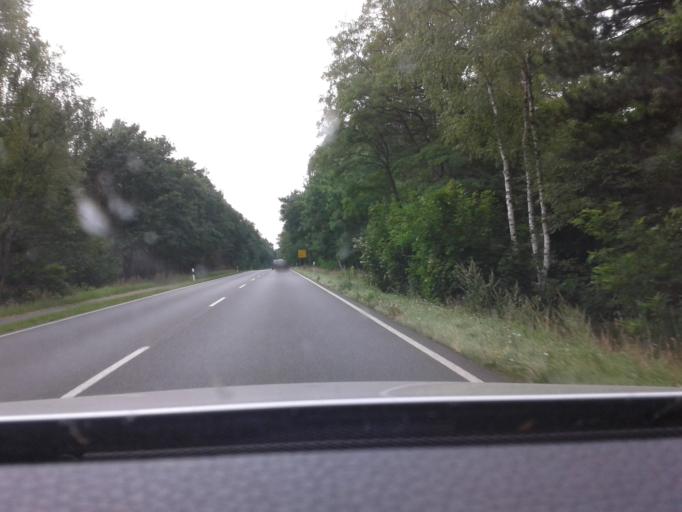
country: DE
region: Lower Saxony
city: Leiferde
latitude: 52.4786
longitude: 10.4416
